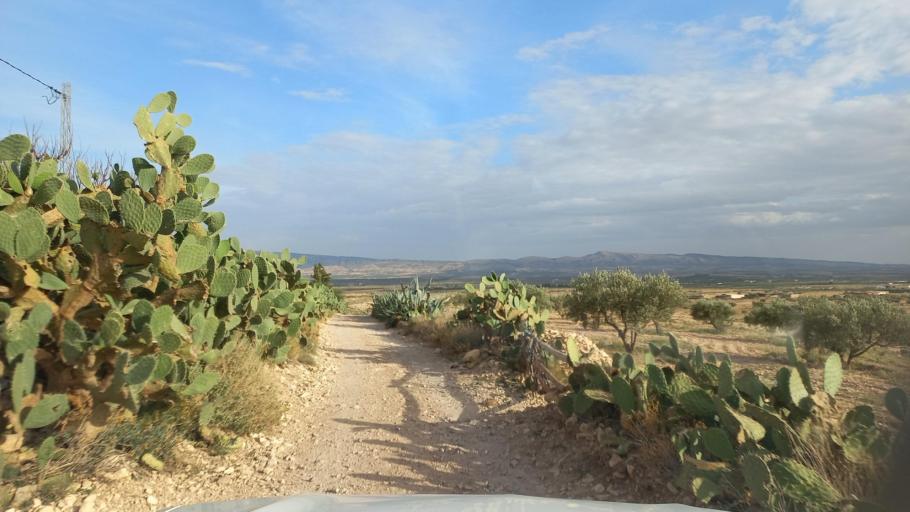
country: TN
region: Al Qasrayn
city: Sbiba
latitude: 35.4545
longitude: 9.0800
